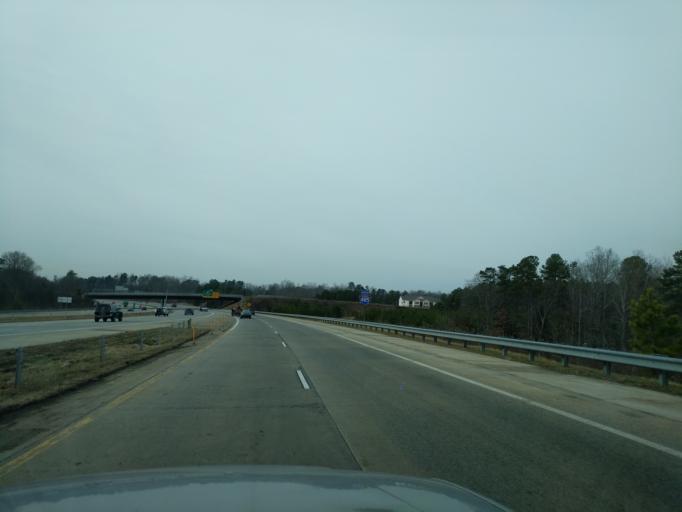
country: US
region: North Carolina
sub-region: Mecklenburg County
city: Huntersville
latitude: 35.3630
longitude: -80.8501
